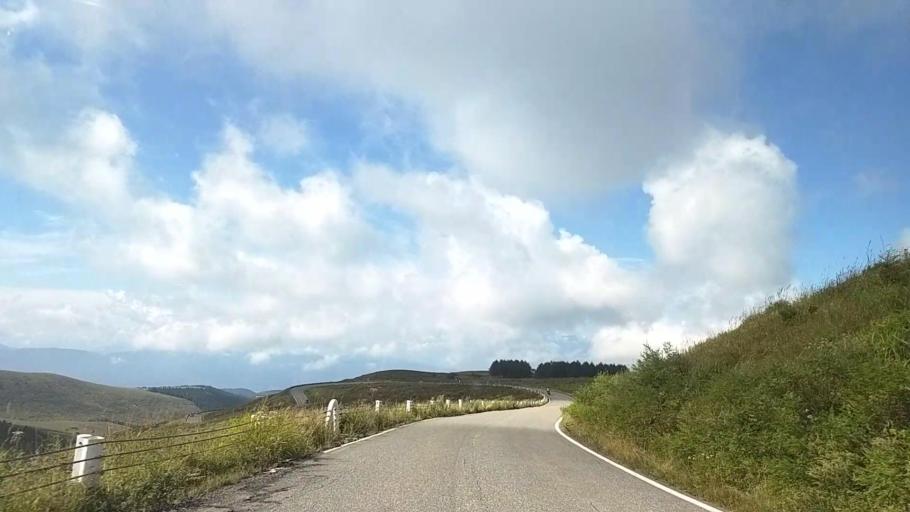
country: JP
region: Nagano
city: Suwa
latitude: 36.1024
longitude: 138.1847
